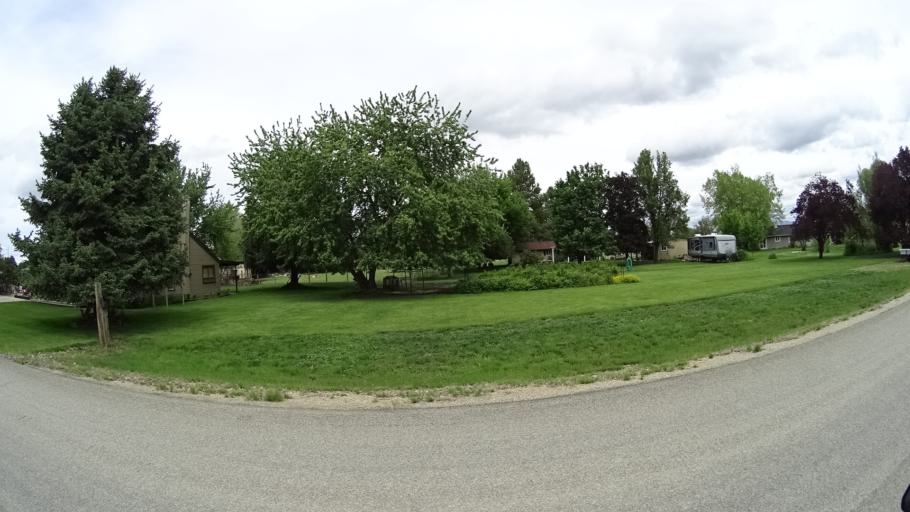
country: US
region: Idaho
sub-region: Ada County
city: Star
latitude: 43.6905
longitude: -116.4319
